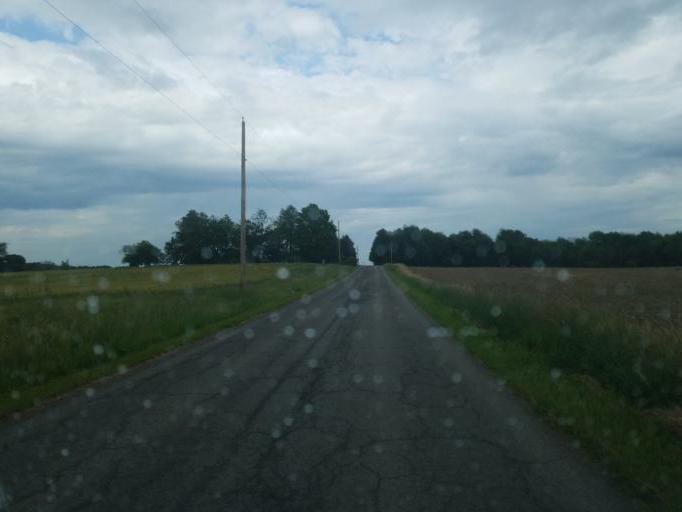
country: US
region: Ohio
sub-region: Richland County
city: Lexington
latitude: 40.6013
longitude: -82.6861
